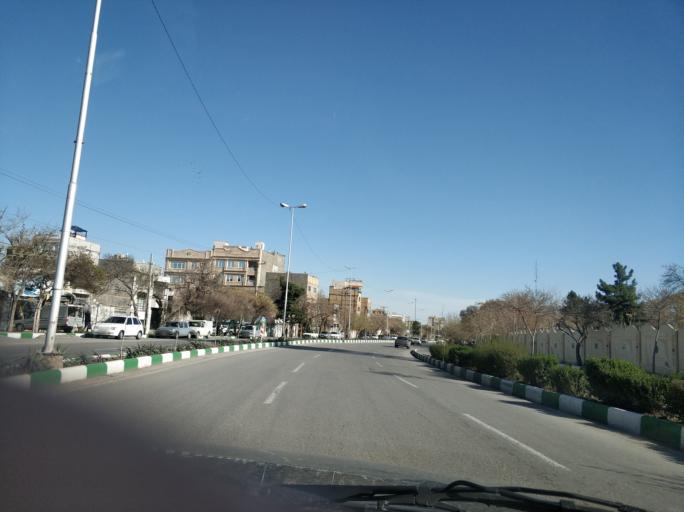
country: IR
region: Razavi Khorasan
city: Mashhad
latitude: 36.3015
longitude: 59.6314
